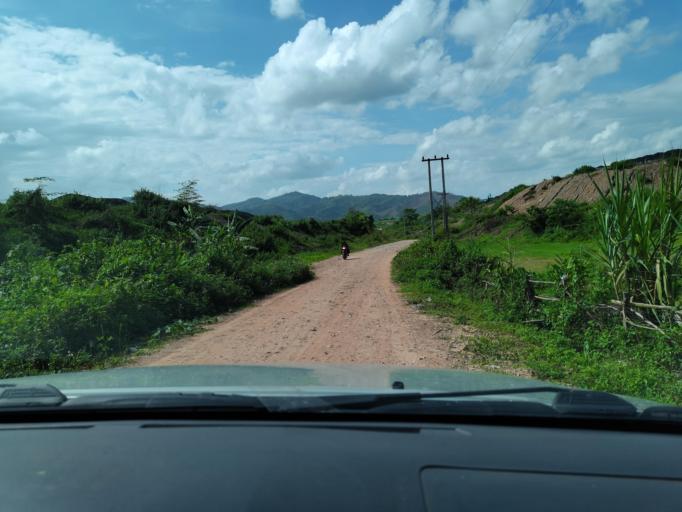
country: LA
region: Loungnamtha
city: Muang Nale
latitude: 20.5818
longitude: 101.0594
